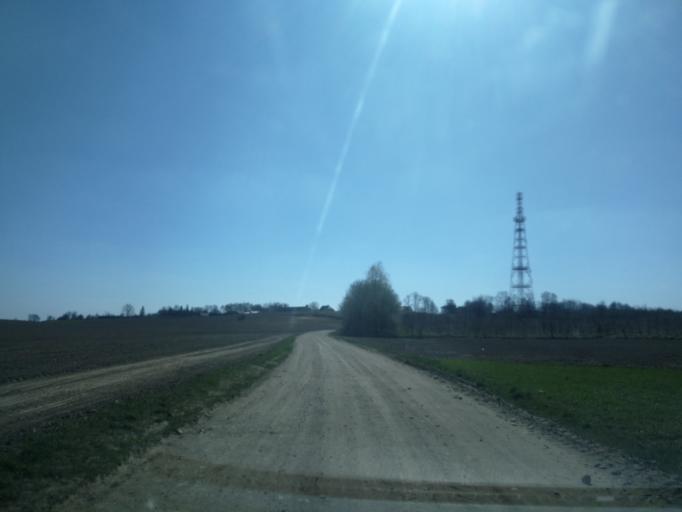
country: PL
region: Warmian-Masurian Voivodeship
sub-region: Powiat ostrodzki
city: Dabrowno
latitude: 53.4413
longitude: 19.9792
